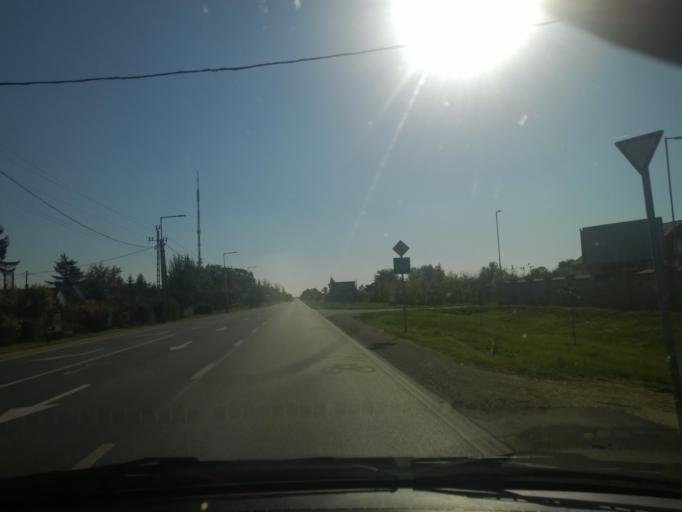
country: HU
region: Csongrad
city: Szentes
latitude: 46.6309
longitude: 20.2749
